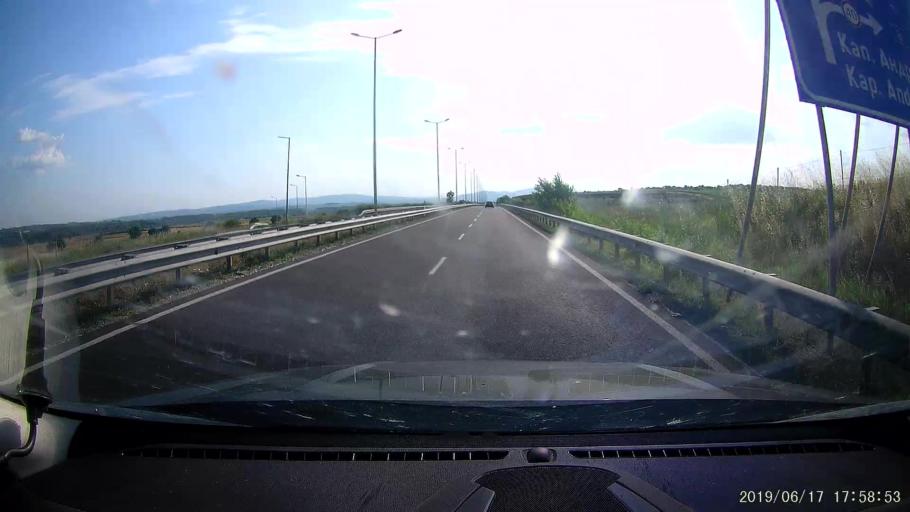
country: BG
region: Khaskovo
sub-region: Obshtina Svilengrad
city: Svilengrad
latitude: 41.7258
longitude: 26.3117
